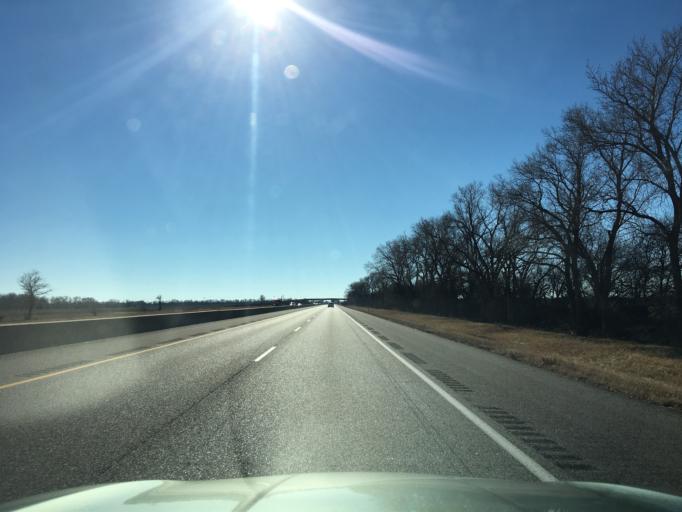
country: US
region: Kansas
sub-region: Sumner County
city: Belle Plaine
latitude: 37.4419
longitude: -97.3218
